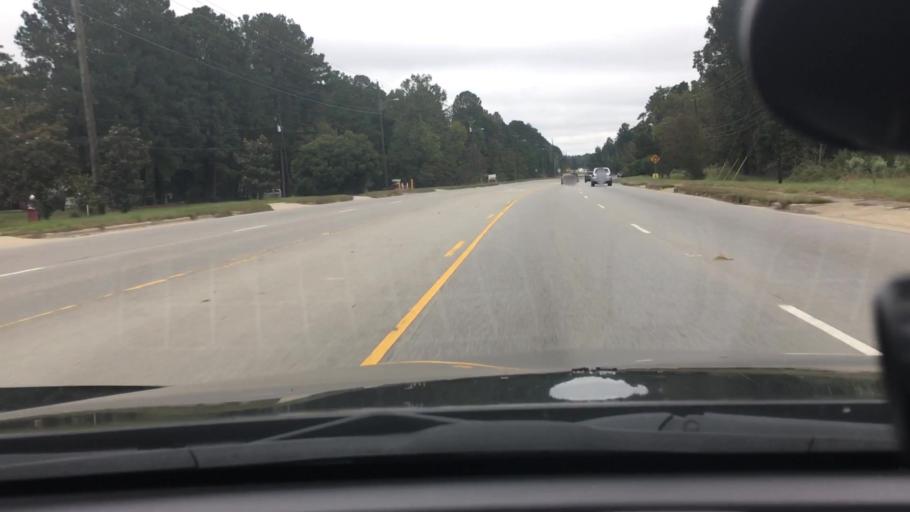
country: US
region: North Carolina
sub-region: Wake County
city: Apex
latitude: 35.6993
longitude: -78.8336
